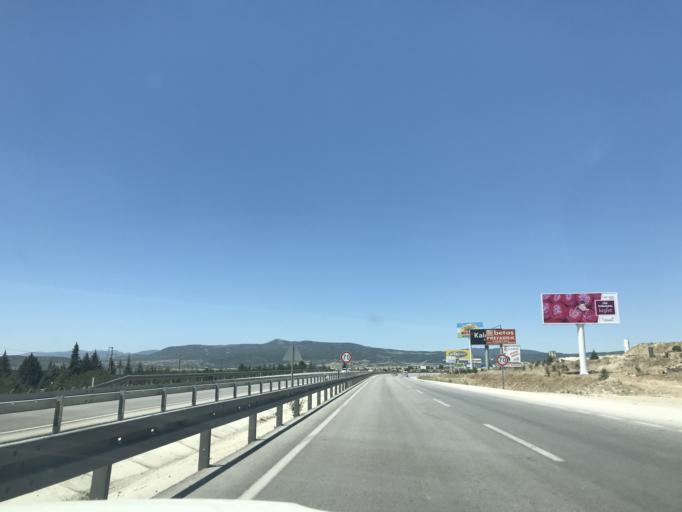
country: TR
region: Isparta
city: Keciborlu
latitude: 37.8946
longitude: 30.3999
